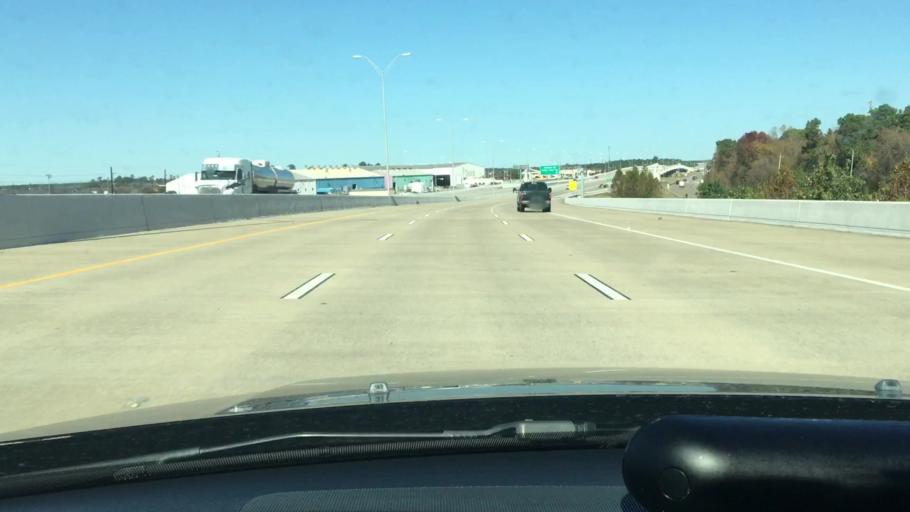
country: US
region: Texas
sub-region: Harris County
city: Sheldon
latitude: 29.8449
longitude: -95.1861
